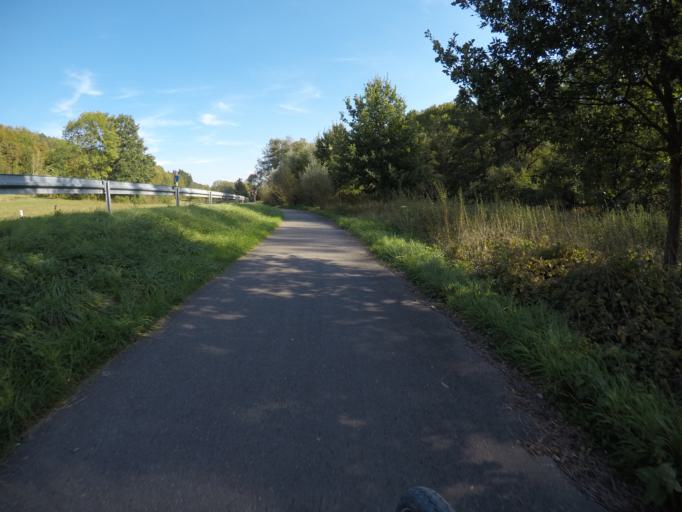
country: DE
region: Baden-Wuerttemberg
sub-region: Regierungsbezirk Stuttgart
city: Schlaitdorf
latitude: 48.6292
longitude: 9.1934
